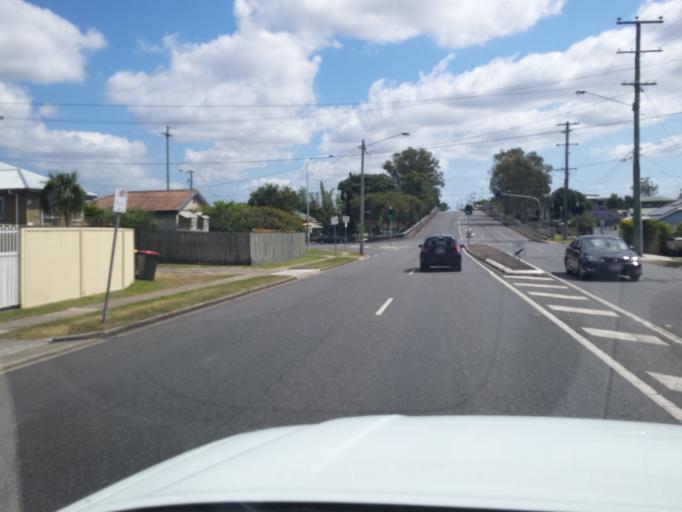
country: AU
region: Queensland
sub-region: Brisbane
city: Zillmere
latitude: -27.3624
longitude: 153.0376
